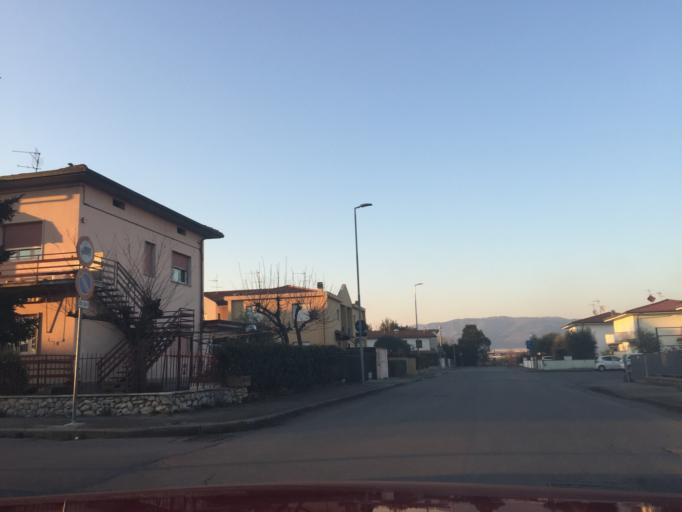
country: IT
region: Tuscany
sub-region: Provincia di Pistoia
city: Ponte Buggianese
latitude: 43.8425
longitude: 10.7512
